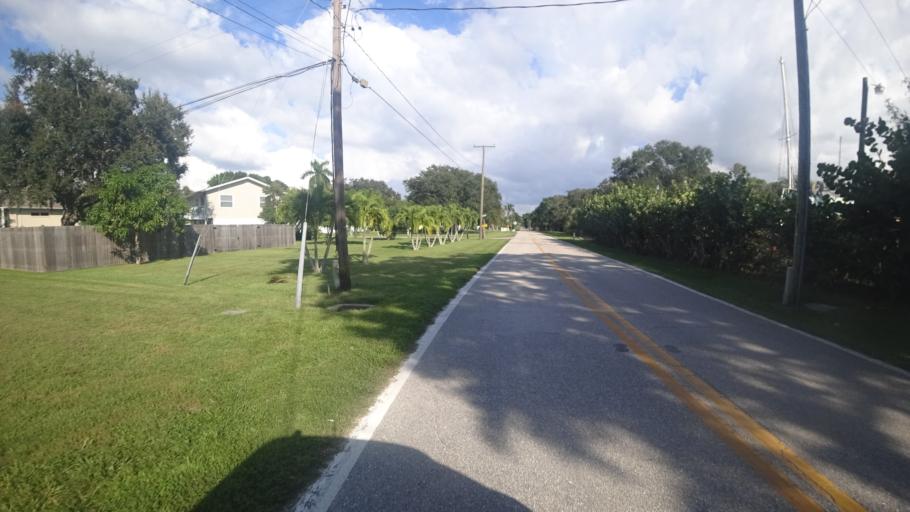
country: US
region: Florida
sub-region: Manatee County
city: West Bradenton
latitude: 27.5262
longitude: -82.6199
